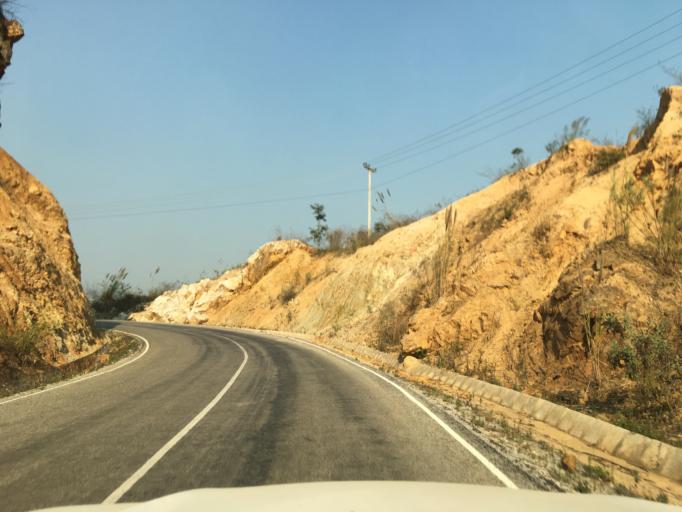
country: LA
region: Houaphan
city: Xam Nua
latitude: 20.5673
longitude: 104.0606
